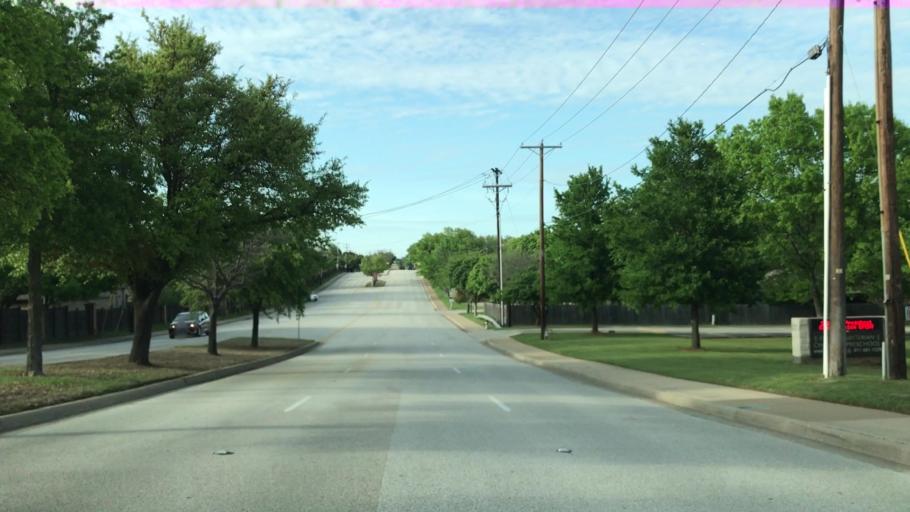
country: US
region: Texas
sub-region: Tarrant County
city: Grapevine
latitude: 32.9511
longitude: -97.0982
